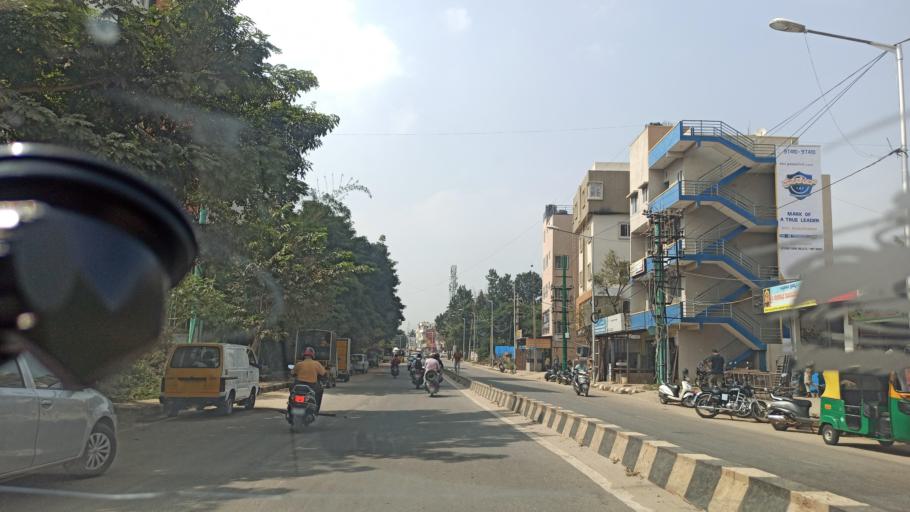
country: IN
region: Karnataka
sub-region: Bangalore Urban
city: Yelahanka
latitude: 13.1045
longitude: 77.6104
